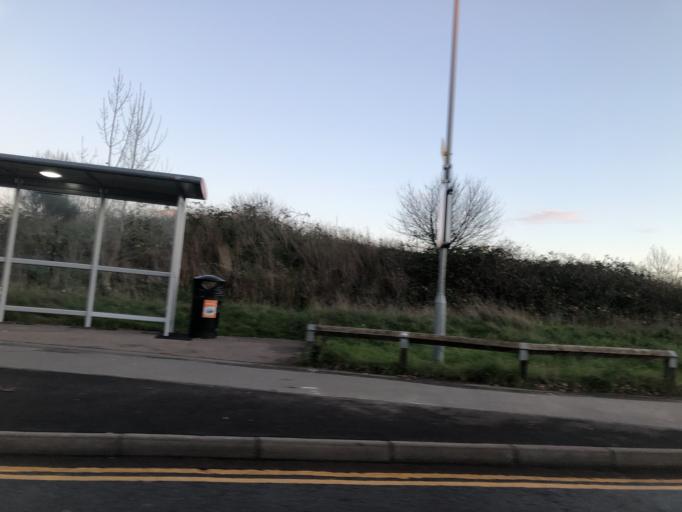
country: GB
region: England
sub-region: Greater London
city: Woolwich
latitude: 51.4785
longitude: 0.0521
